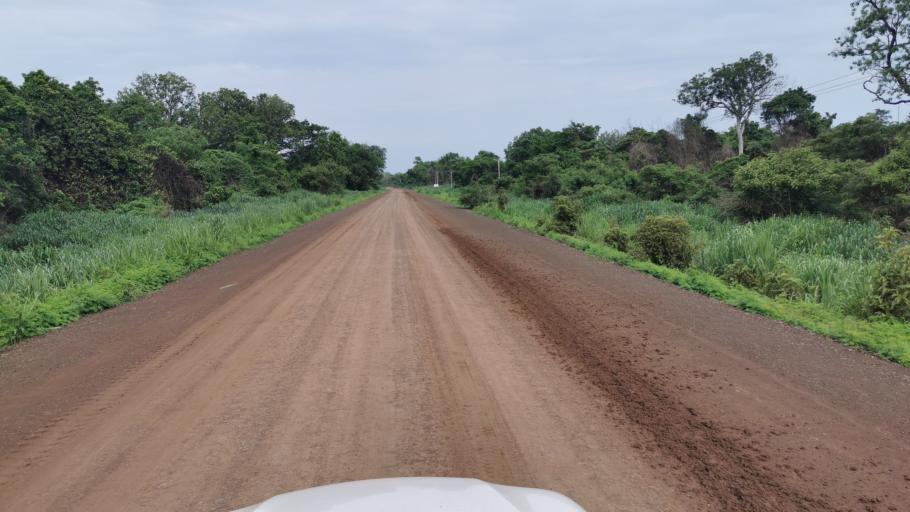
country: ET
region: Gambela
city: Gambela
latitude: 7.8352
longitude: 34.5049
